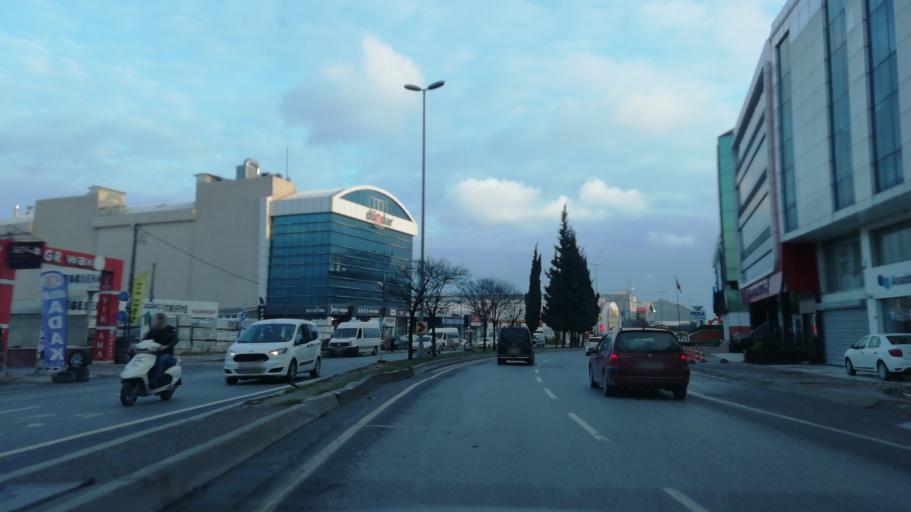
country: TR
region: Istanbul
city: Yakuplu
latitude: 41.0007
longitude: 28.7122
